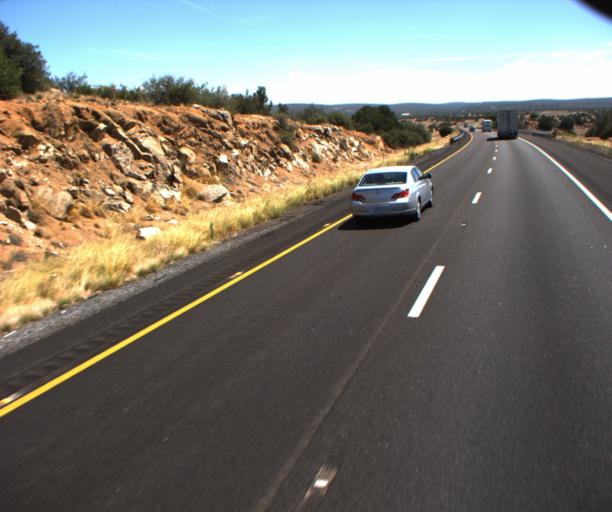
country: US
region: Arizona
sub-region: Mohave County
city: Peach Springs
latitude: 35.1851
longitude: -113.3824
